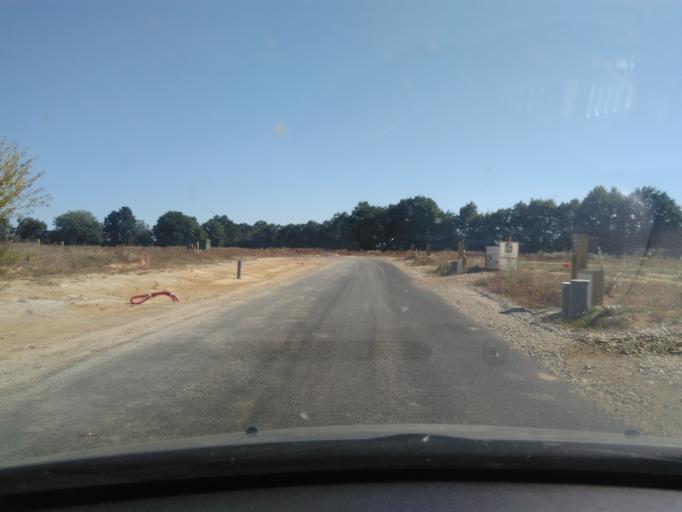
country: FR
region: Pays de la Loire
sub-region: Departement de la Vendee
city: Mouilleron-le-Captif
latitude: 46.7173
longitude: -1.4704
